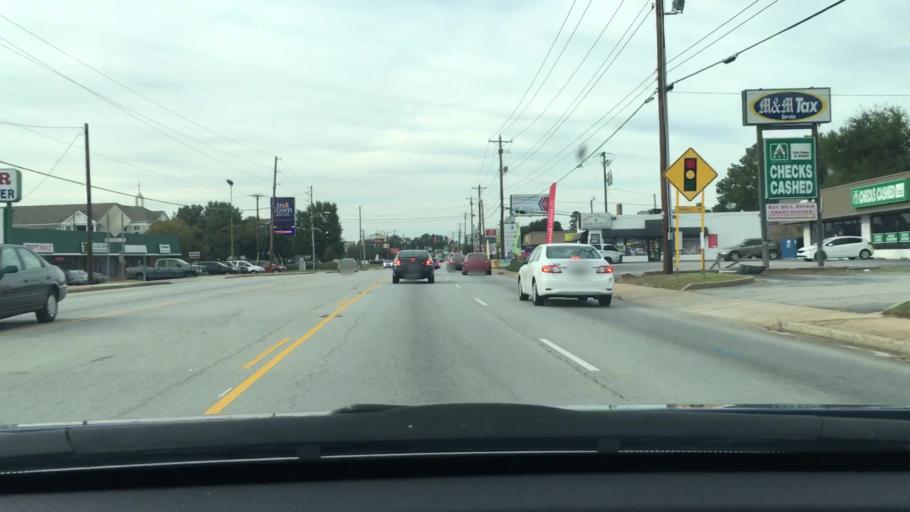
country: US
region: South Carolina
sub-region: Lexington County
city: West Columbia
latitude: 34.0320
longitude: -81.0874
